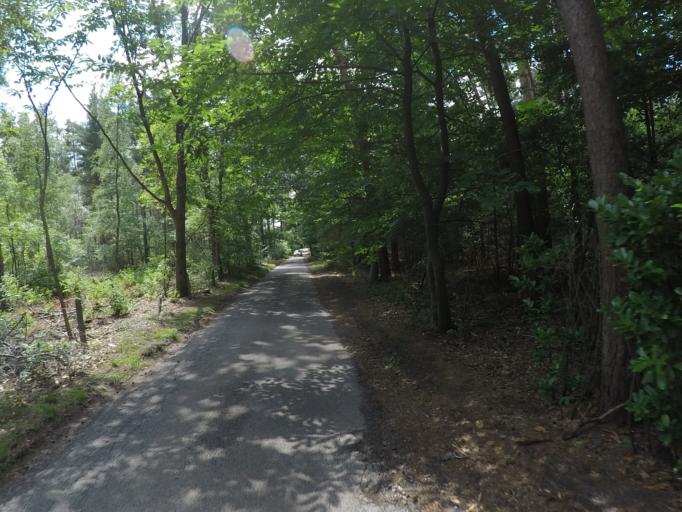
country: BE
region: Flanders
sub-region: Provincie Antwerpen
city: Vosselaar
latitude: 51.3225
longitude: 4.8881
